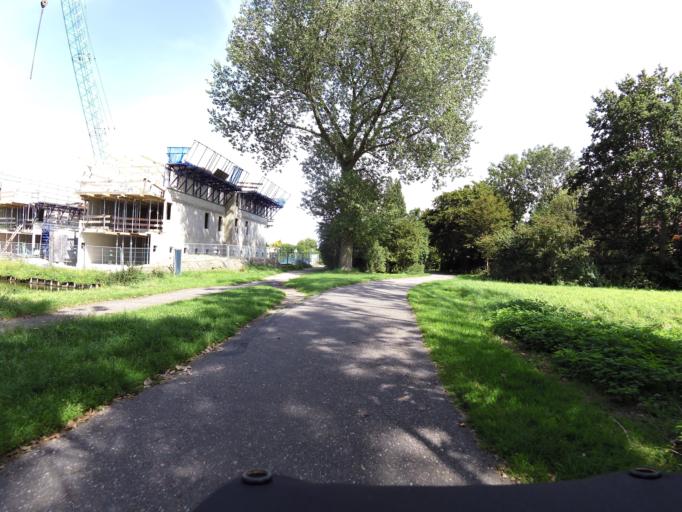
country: NL
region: South Holland
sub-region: Gemeente Goeree-Overflakkee
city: Middelharnis
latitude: 51.7545
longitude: 4.1458
